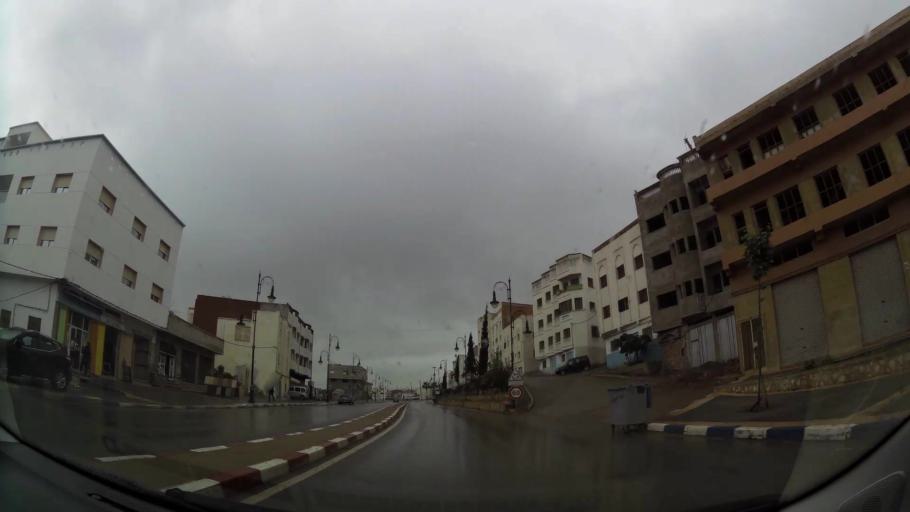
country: MA
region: Taza-Al Hoceima-Taounate
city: Imzourene
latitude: 35.1448
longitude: -3.8482
